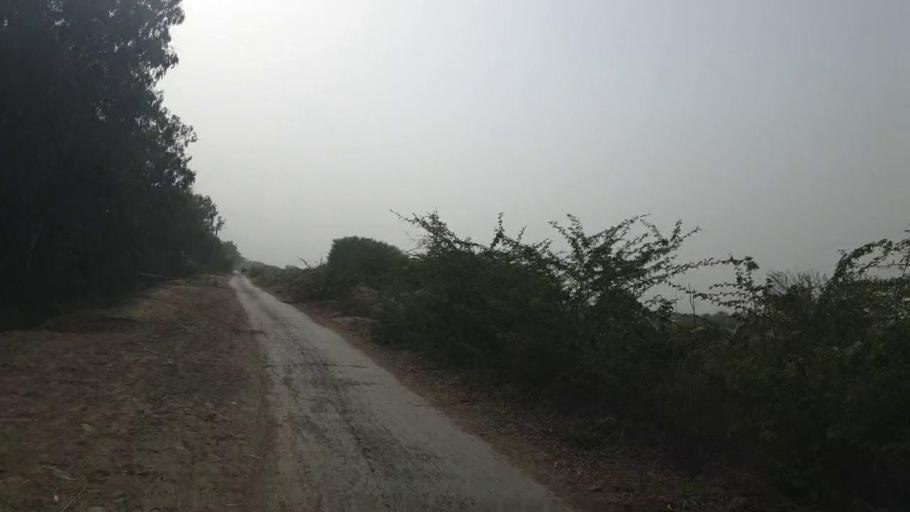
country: PK
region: Sindh
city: Kunri
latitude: 25.0694
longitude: 69.4985
